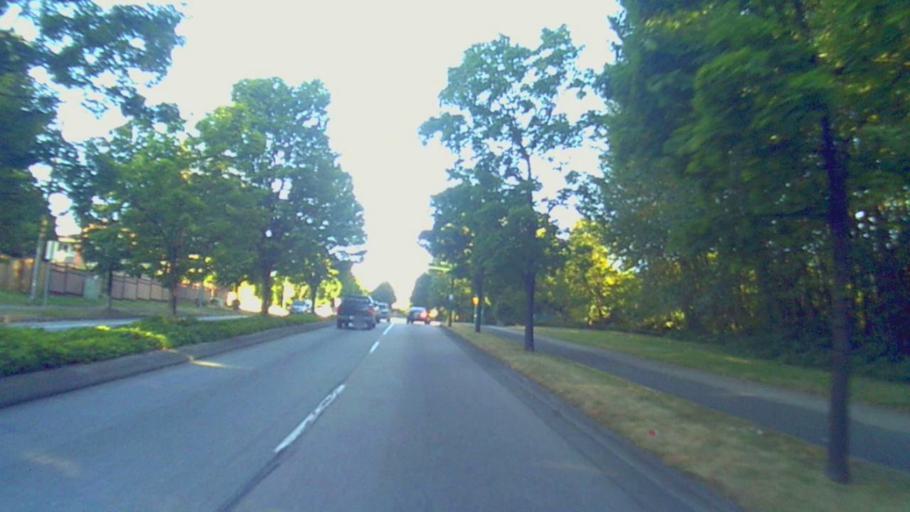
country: CA
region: British Columbia
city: New Westminster
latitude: 49.2388
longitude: -122.9070
